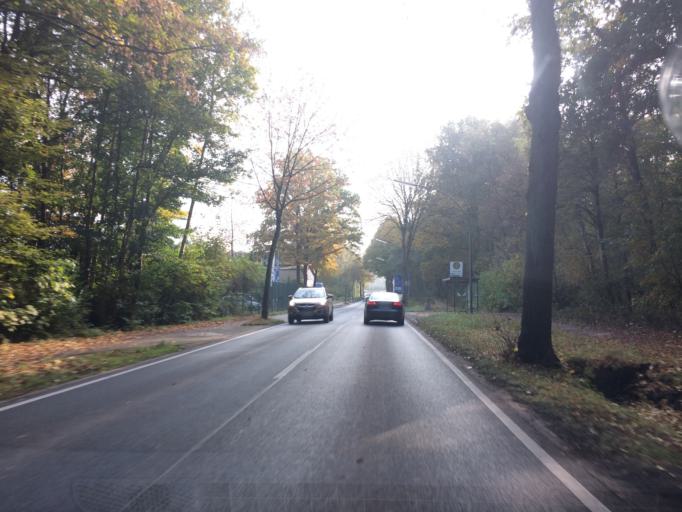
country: DE
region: North Rhine-Westphalia
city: Marl
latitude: 51.6767
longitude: 7.0755
